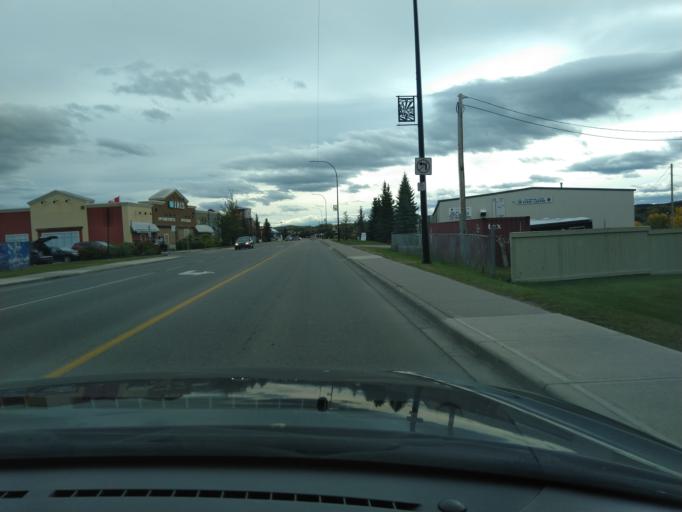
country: CA
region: Alberta
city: Cochrane
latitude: 51.1903
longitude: -114.4748
